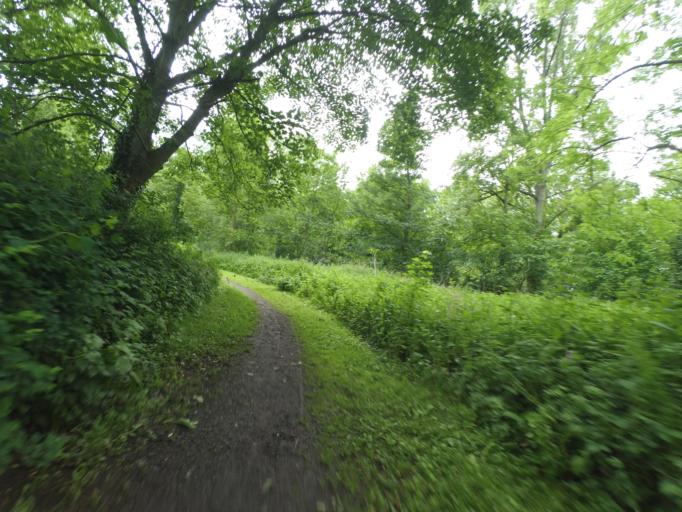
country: GB
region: Scotland
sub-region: East Lothian
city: Pencaitland
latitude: 55.9118
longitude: -2.8950
